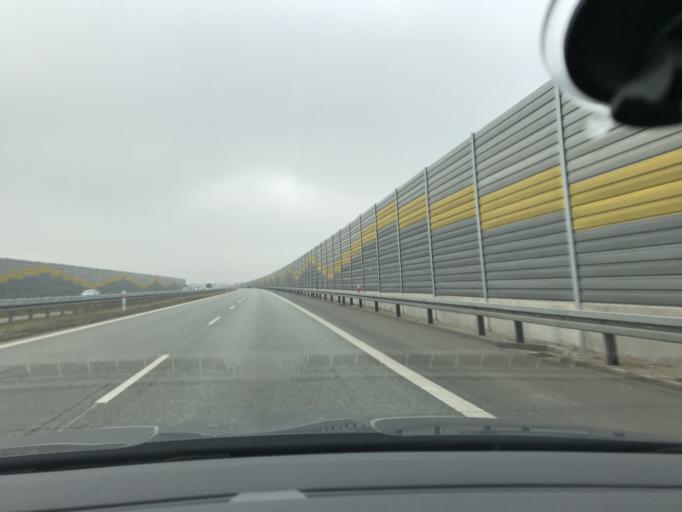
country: PL
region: Lodz Voivodeship
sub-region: Powiat pabianicki
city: Dobron
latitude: 51.5927
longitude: 19.2206
